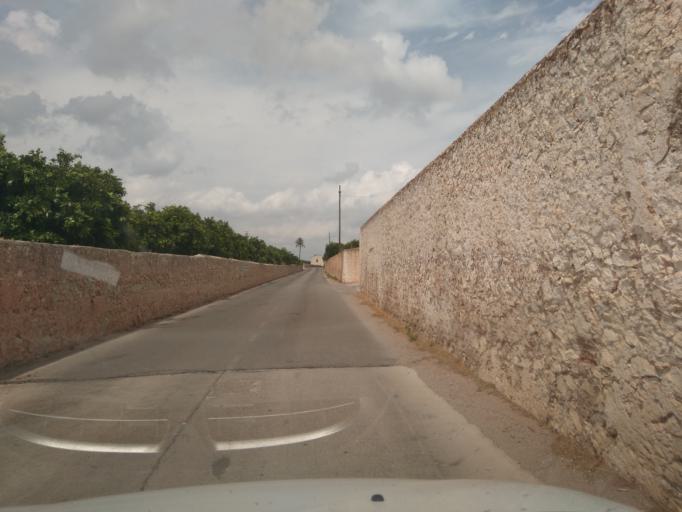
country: ES
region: Valencia
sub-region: Provincia de Valencia
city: Carcaixent
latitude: 39.1122
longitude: -0.4371
